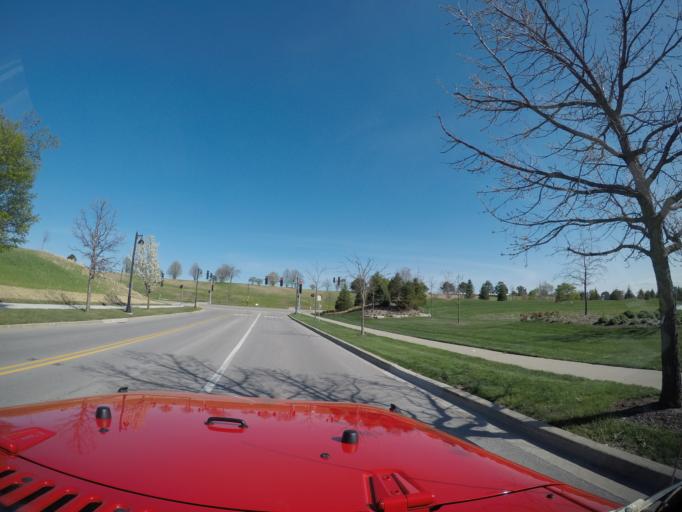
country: US
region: Illinois
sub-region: Cook County
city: Northbrook
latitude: 42.0905
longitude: -87.8313
